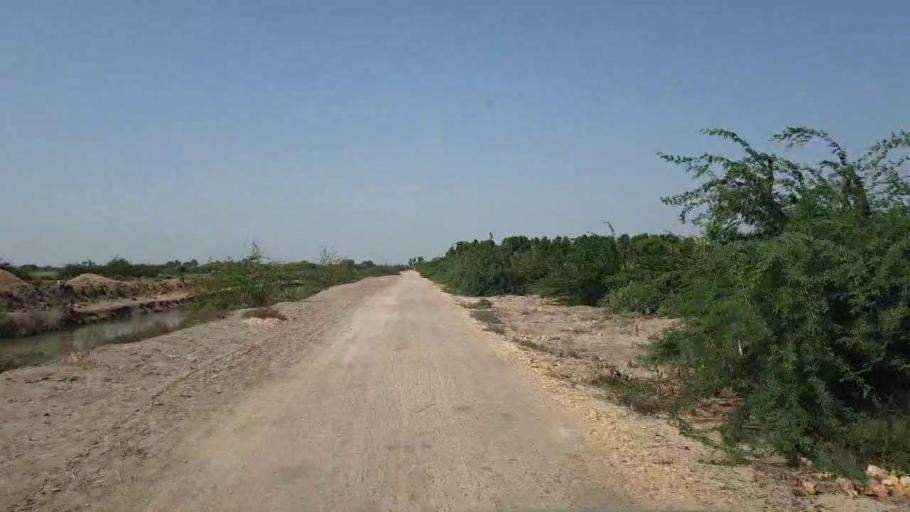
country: PK
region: Sindh
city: Tando Bago
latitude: 24.7419
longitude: 69.0714
